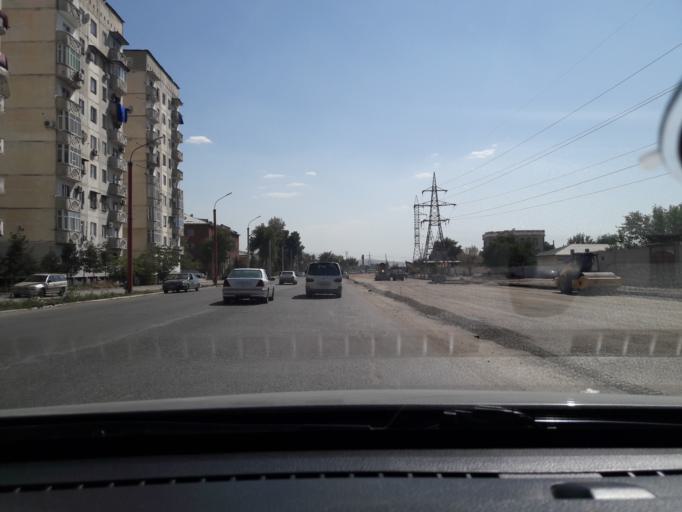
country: TJ
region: Dushanbe
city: Dushanbe
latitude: 38.5344
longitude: 68.7389
